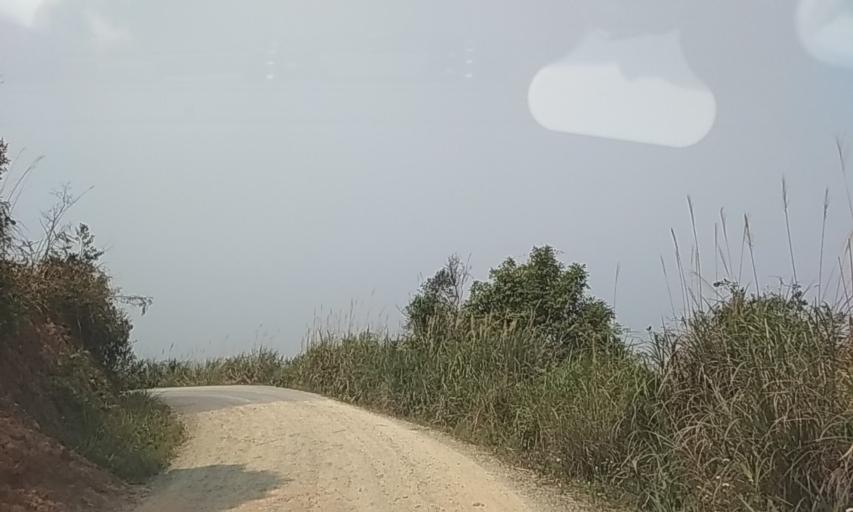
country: TH
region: Nan
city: Chaloem Phra Kiat
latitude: 20.0525
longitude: 101.0756
